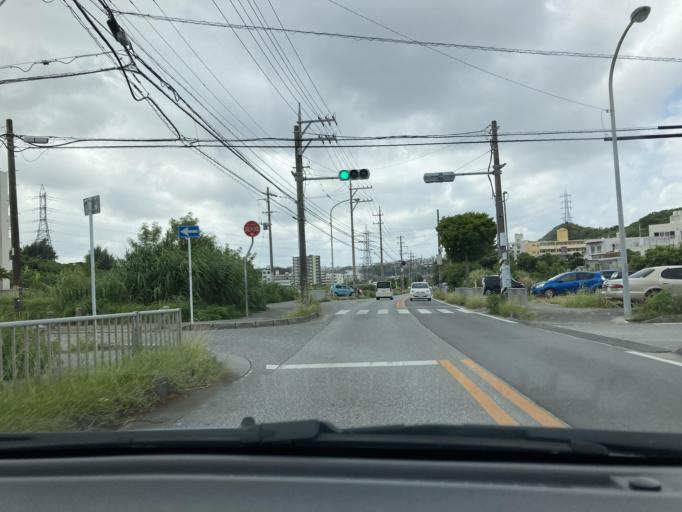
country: JP
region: Okinawa
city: Ginowan
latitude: 26.2411
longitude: 127.7524
